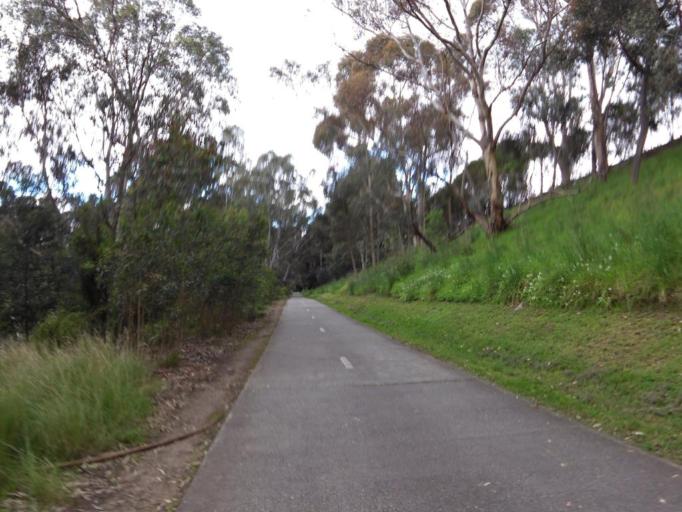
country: AU
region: Victoria
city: Alphington
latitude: -37.7900
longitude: 145.0368
